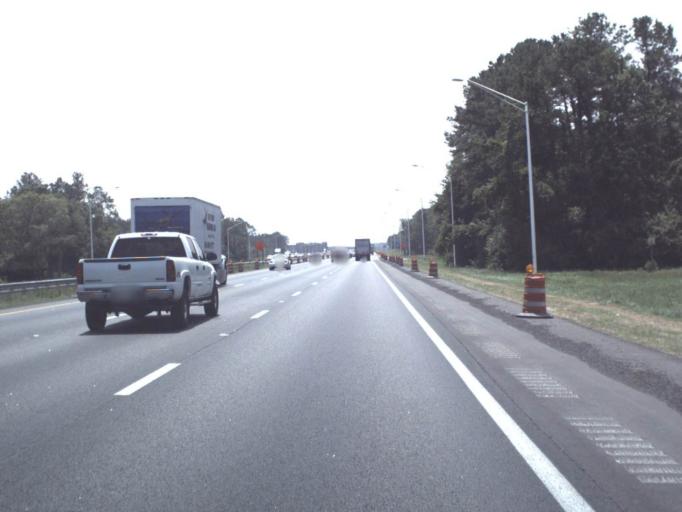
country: US
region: Florida
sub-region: Saint Johns County
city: Fruit Cove
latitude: 30.1284
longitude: -81.5280
